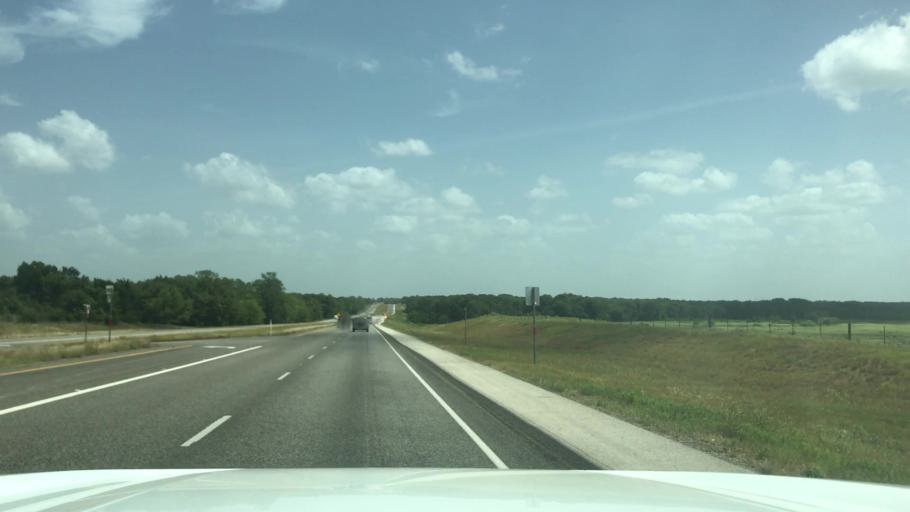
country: US
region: Texas
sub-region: Robertson County
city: Calvert
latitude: 30.9511
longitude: -96.6513
